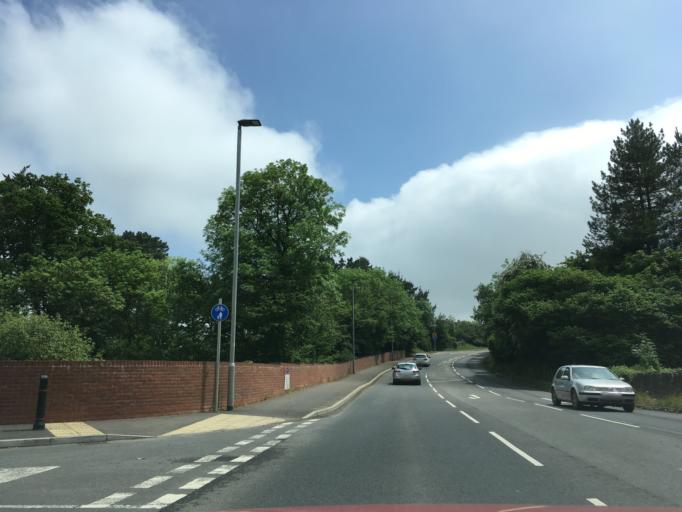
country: GB
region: England
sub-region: Devon
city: Totnes
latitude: 50.4399
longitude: -3.6962
